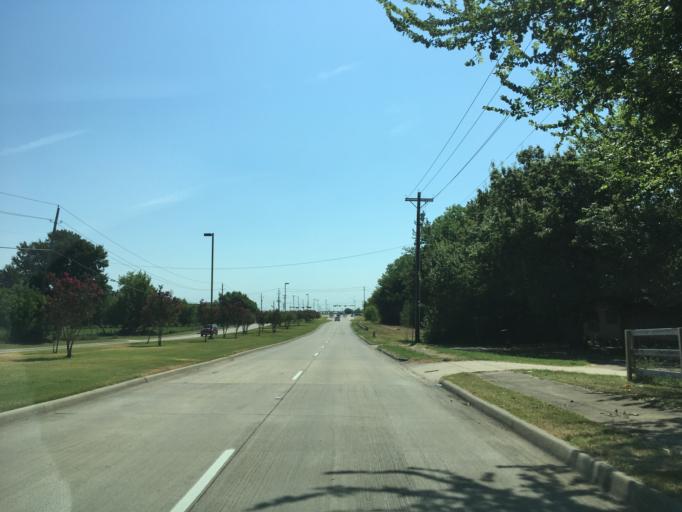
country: US
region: Texas
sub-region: Collin County
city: Fairview
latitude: 33.1590
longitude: -96.6671
